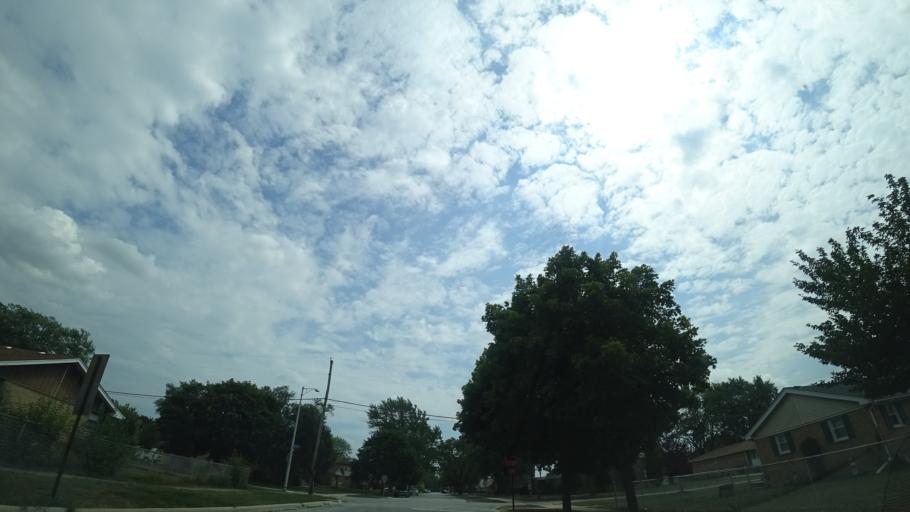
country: US
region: Illinois
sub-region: Cook County
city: Chicago Ridge
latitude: 41.6980
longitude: -87.7719
